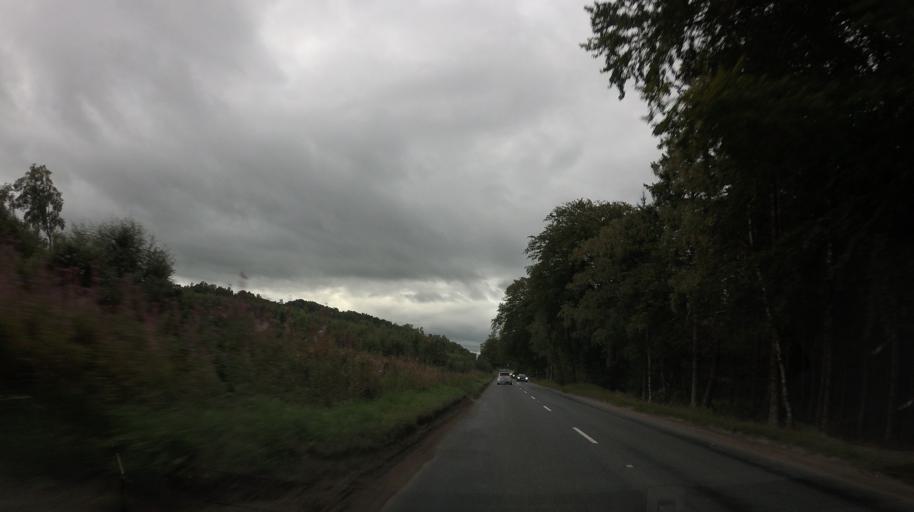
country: GB
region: Scotland
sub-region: Aberdeenshire
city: Kemnay
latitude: 57.1759
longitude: -2.4327
